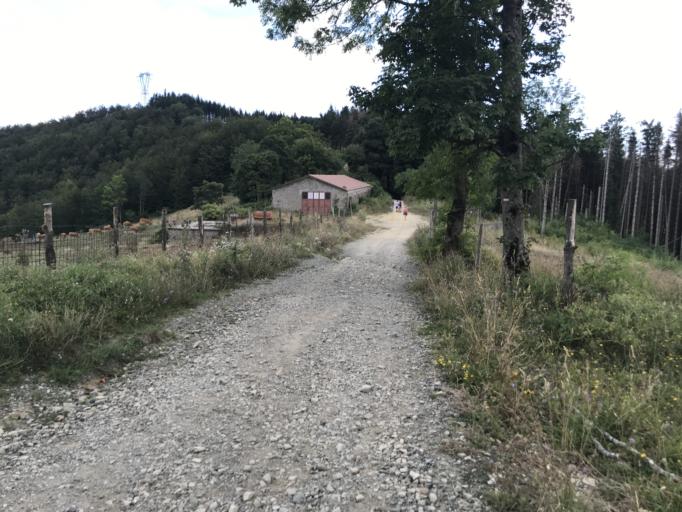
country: IT
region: Emilia-Romagna
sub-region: Provincia di Bologna
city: San Benedetto Val di Sambro
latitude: 44.1536
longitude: 11.2624
